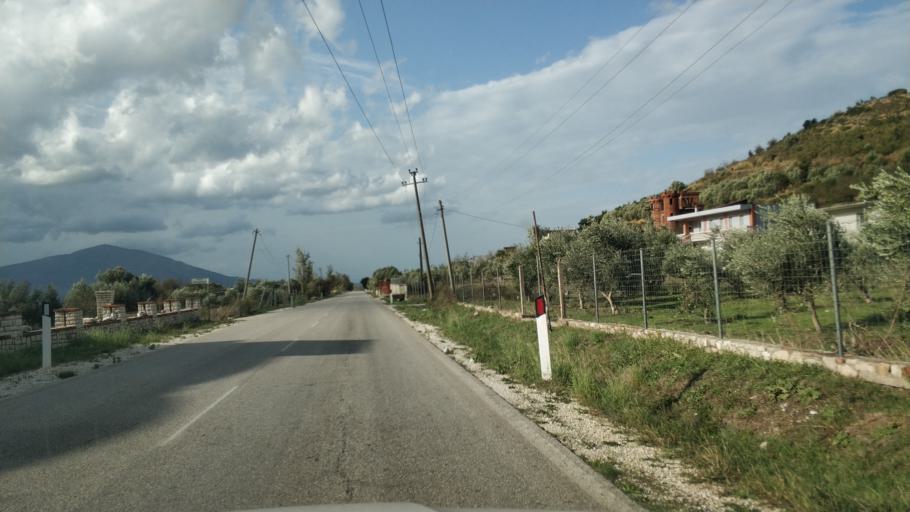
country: AL
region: Vlore
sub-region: Rrethi i Vlores
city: Orikum
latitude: 40.2993
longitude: 19.4866
